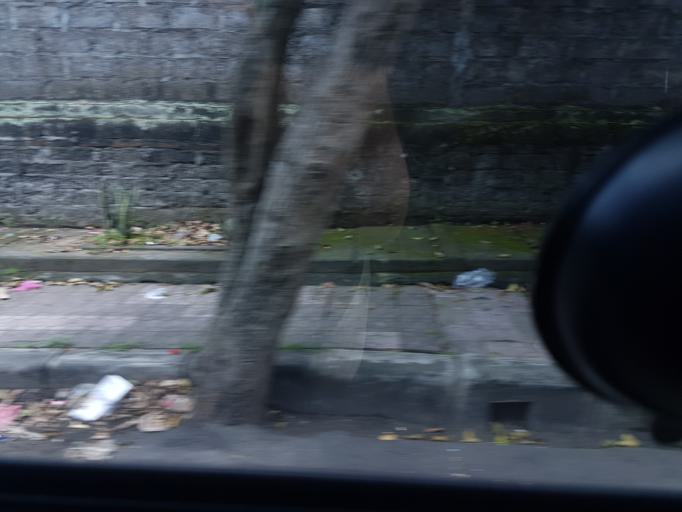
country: ID
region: Bali
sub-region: Kabupaten Gianyar
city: Ubud
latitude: -8.5128
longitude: 115.2934
